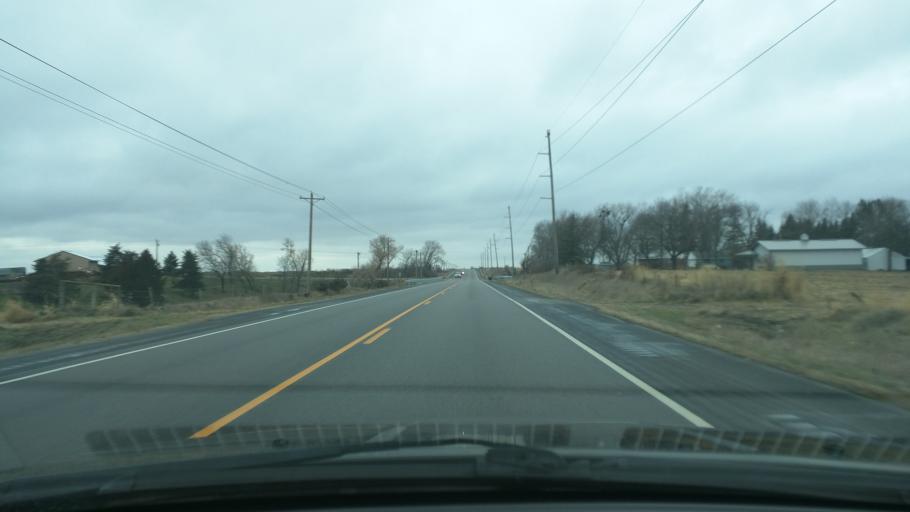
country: US
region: Minnesota
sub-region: Dakota County
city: Hastings
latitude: 44.7384
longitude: -92.9261
